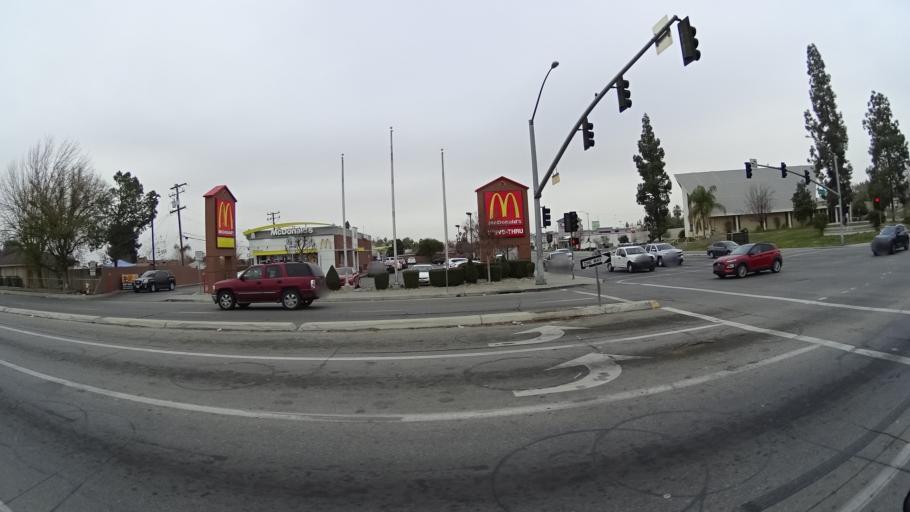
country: US
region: California
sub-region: Kern County
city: Bakersfield
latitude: 35.3756
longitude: -118.9496
